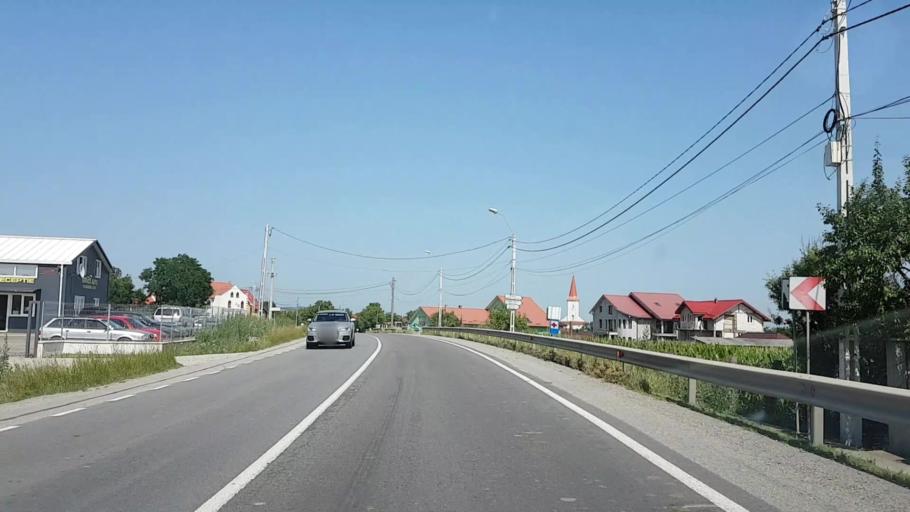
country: RO
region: Cluj
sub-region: Comuna Cusdrioara
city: Cusdrioara
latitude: 47.1694
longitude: 23.9158
